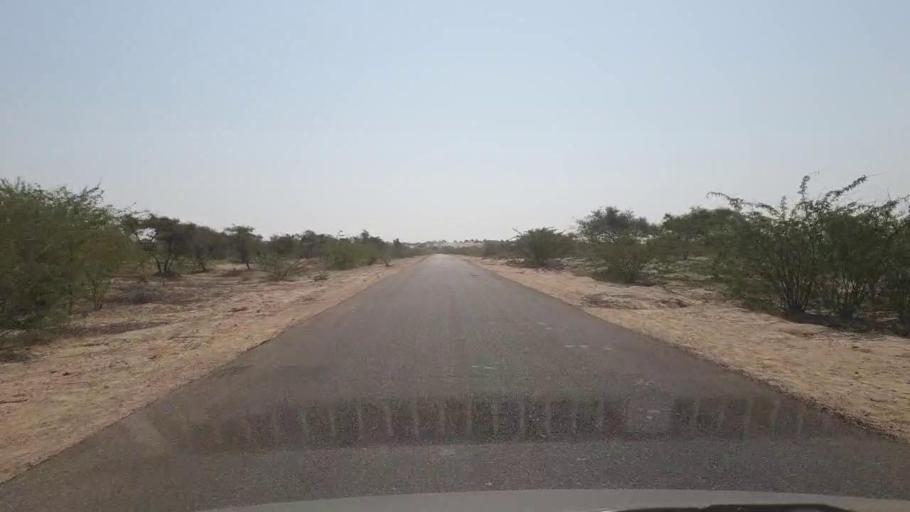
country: PK
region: Sindh
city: Chor
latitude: 25.5901
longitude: 70.1839
